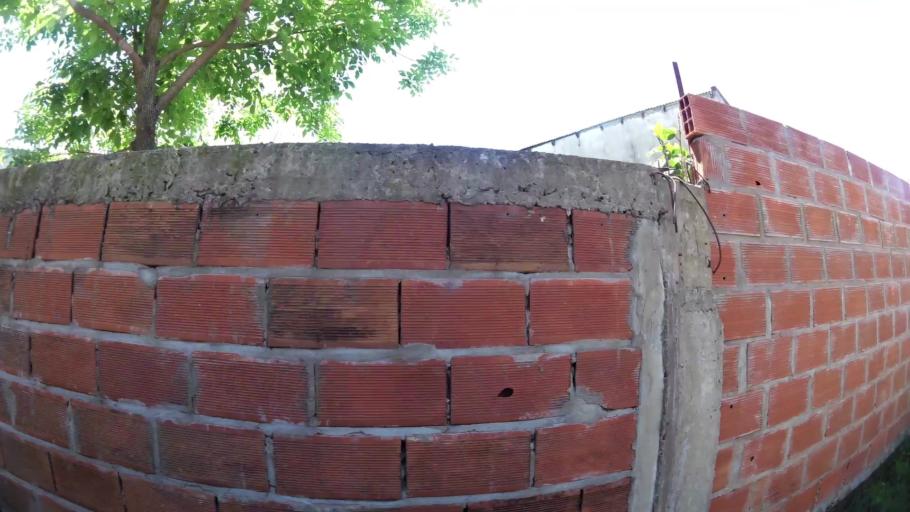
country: AR
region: Buenos Aires
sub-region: Partido de Quilmes
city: Quilmes
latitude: -34.7443
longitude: -58.3073
